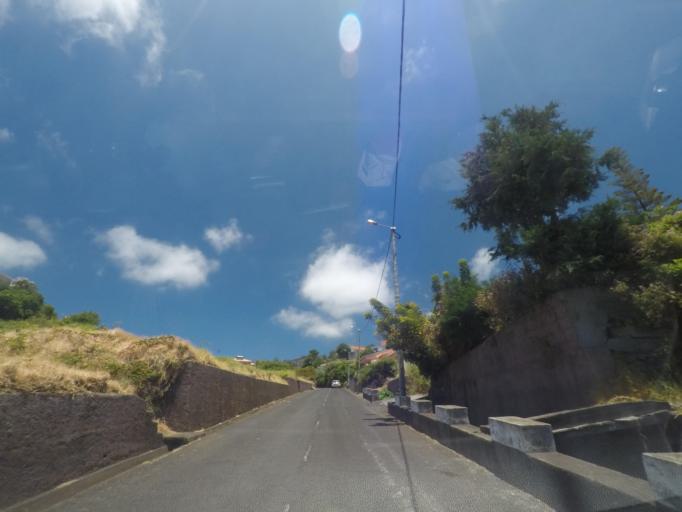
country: PT
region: Madeira
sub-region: Calheta
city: Estreito da Calheta
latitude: 32.7322
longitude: -17.1747
